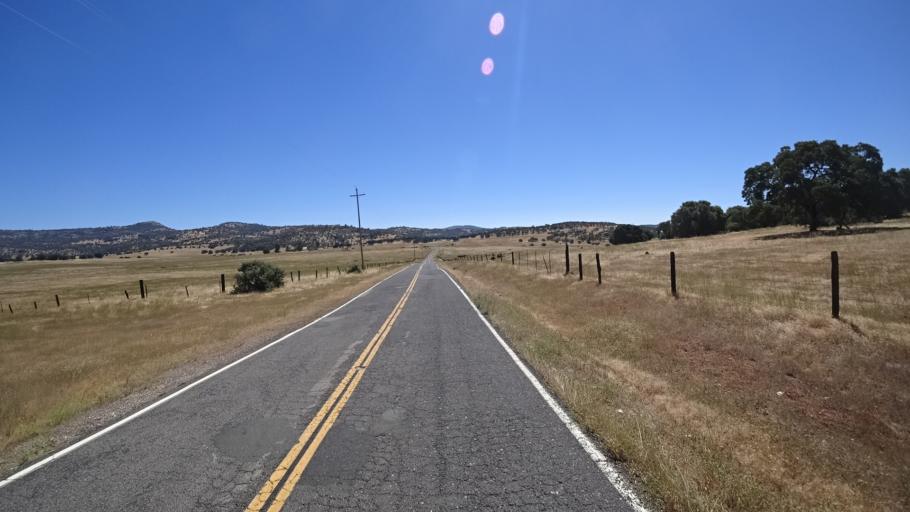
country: US
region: California
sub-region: Calaveras County
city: Copperopolis
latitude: 38.0205
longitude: -120.7039
